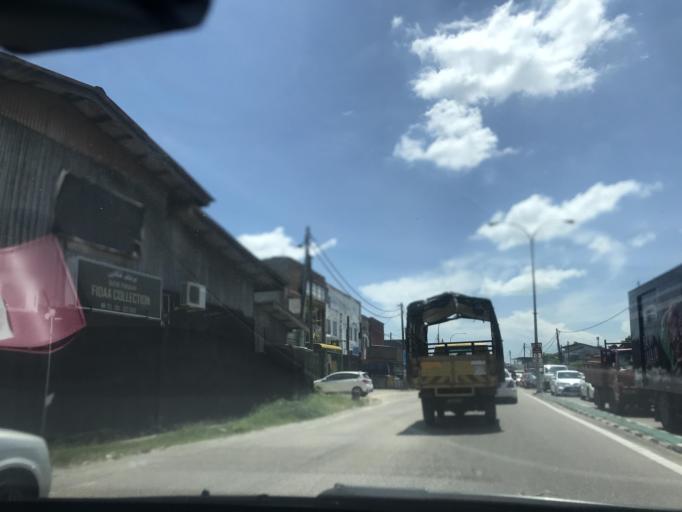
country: MY
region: Kelantan
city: Kota Bharu
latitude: 6.1157
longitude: 102.2683
